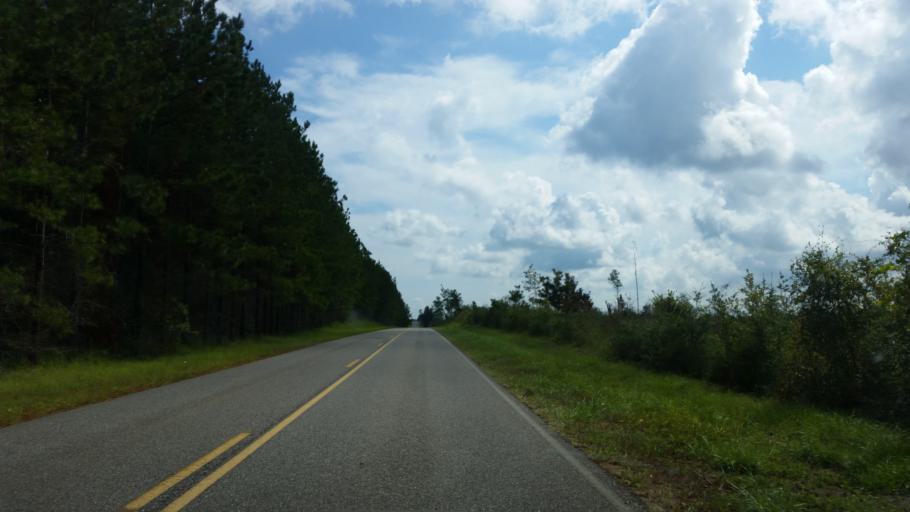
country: US
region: Florida
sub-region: Escambia County
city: Cantonment
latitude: 30.6884
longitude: -87.4546
